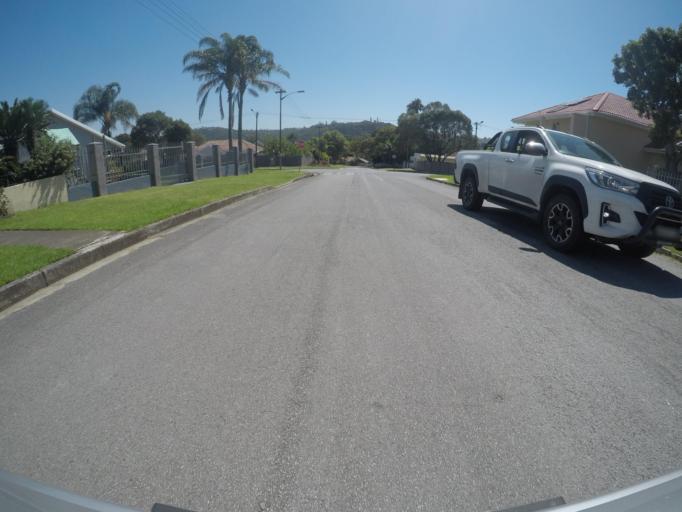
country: ZA
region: Eastern Cape
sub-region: Buffalo City Metropolitan Municipality
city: East London
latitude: -32.9737
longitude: 27.9213
